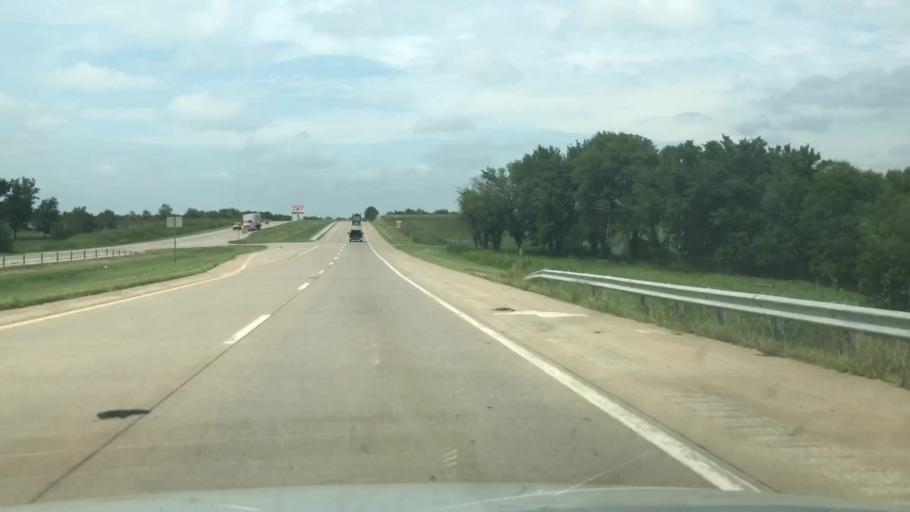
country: US
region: Oklahoma
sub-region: Washington County
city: Bartlesville
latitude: 36.5895
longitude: -95.9324
